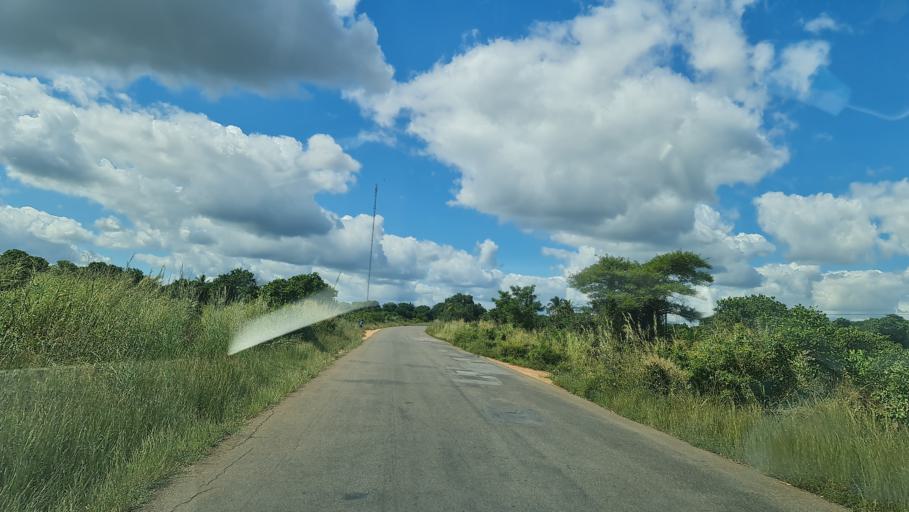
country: MZ
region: Zambezia
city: Quelimane
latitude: -17.5071
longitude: 36.2418
